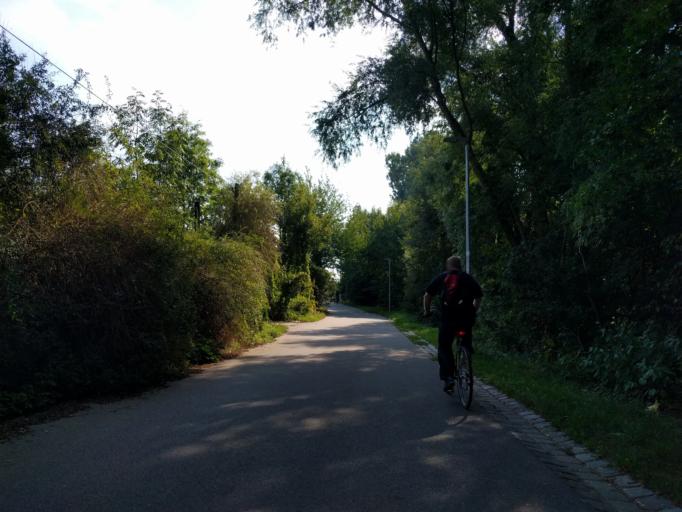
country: DE
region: Bavaria
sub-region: Upper Palatinate
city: Regensburg
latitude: 49.0239
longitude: 12.1265
